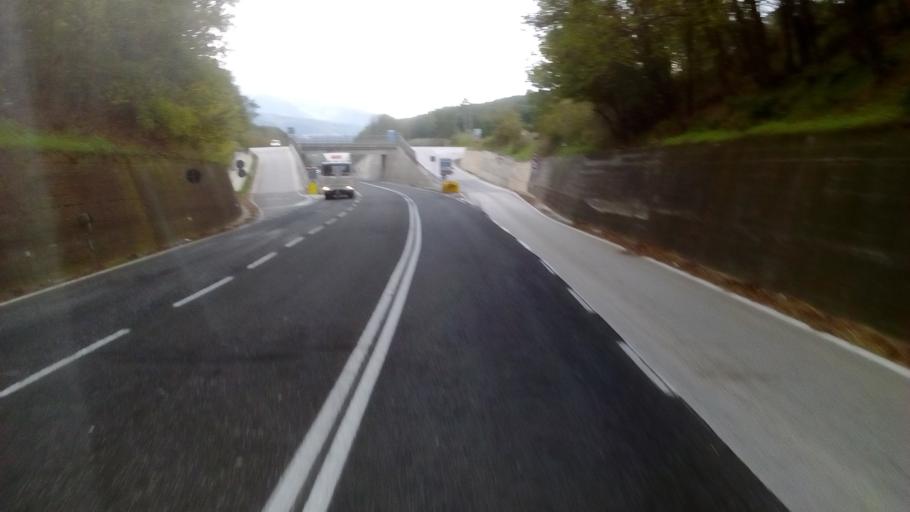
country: IT
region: Molise
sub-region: Provincia di Isernia
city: Isernia
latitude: 41.5905
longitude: 14.2409
